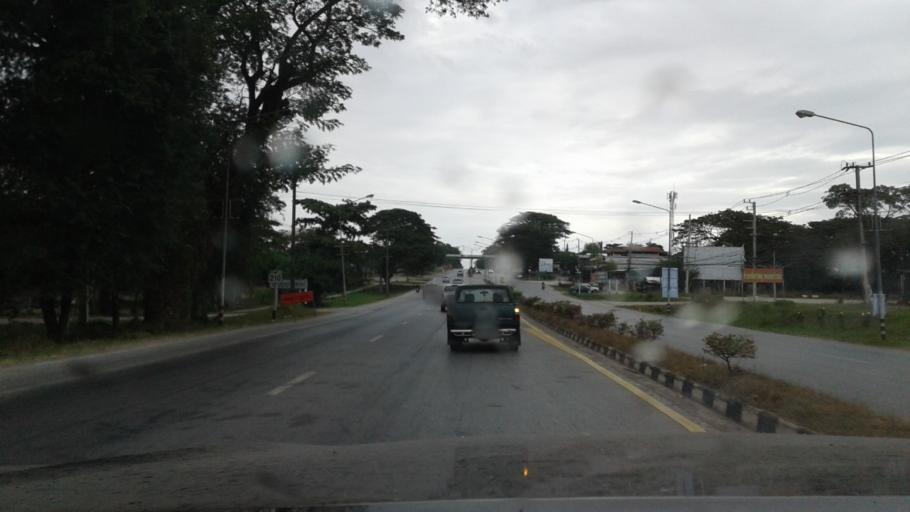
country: TH
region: Changwat Udon Thani
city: Nong Wua So
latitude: 17.2737
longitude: 102.6018
